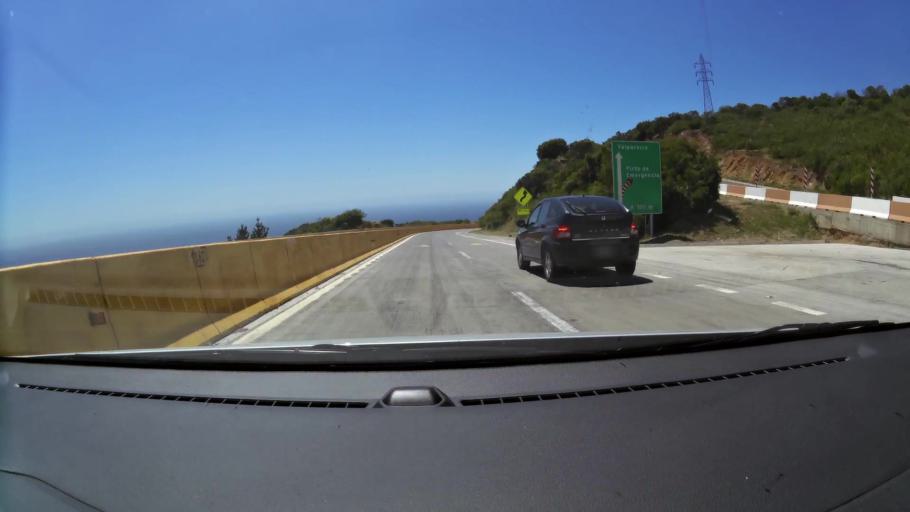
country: CL
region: Valparaiso
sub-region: Provincia de Valparaiso
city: Valparaiso
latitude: -33.0526
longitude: -71.6557
